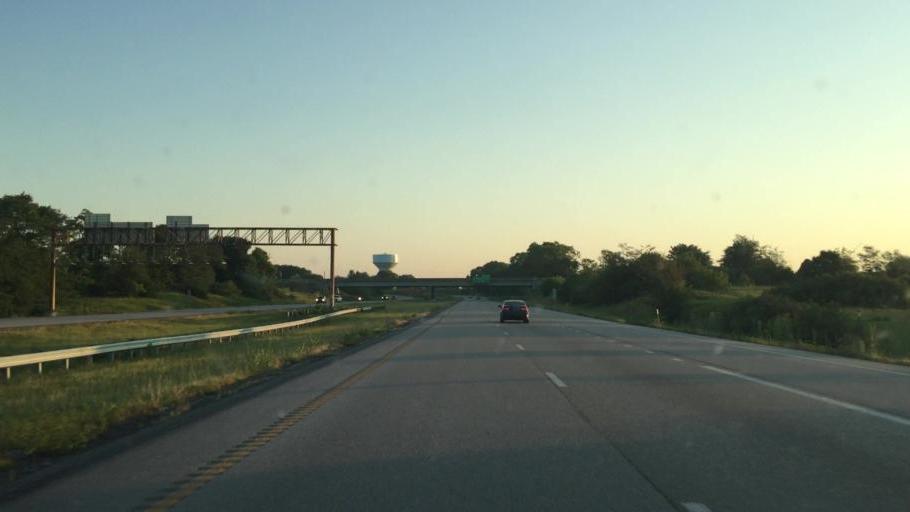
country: US
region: Missouri
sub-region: Clay County
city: Pleasant Valley
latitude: 39.3003
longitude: -94.5100
